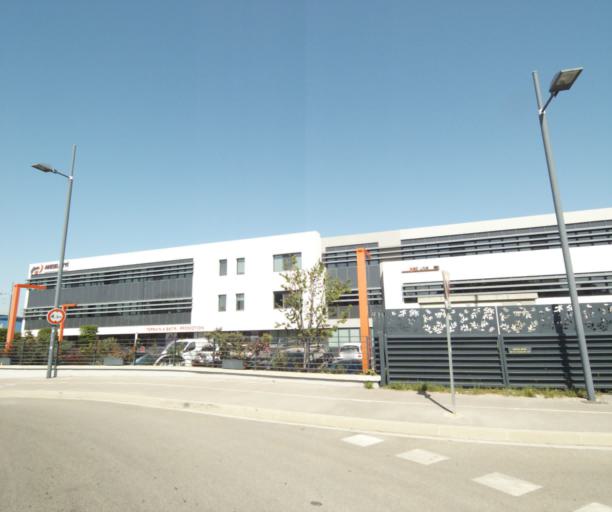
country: FR
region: Languedoc-Roussillon
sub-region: Departement de l'Herault
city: Castelnau-le-Lez
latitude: 43.6266
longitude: 3.9011
